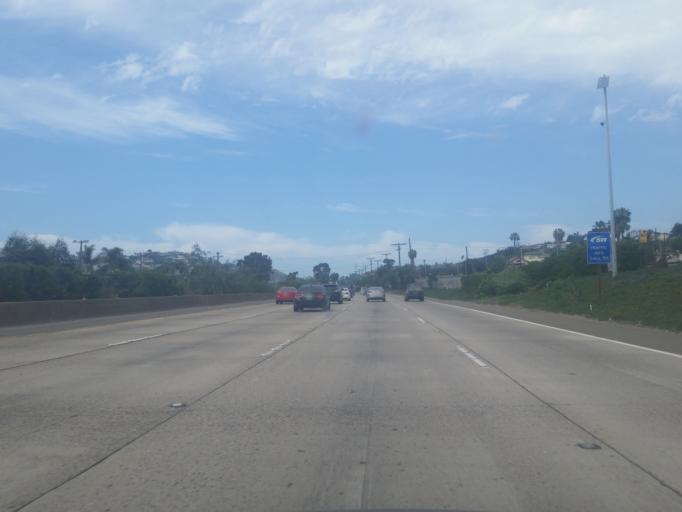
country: US
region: California
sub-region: San Diego County
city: La Jolla
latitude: 32.8009
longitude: -117.2116
